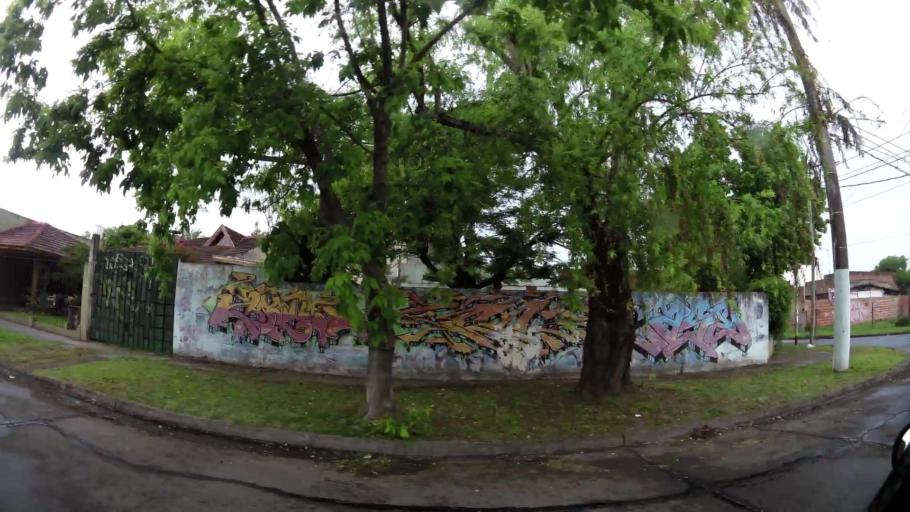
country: AR
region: Buenos Aires
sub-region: Partido de Quilmes
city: Quilmes
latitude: -34.7706
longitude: -58.2158
